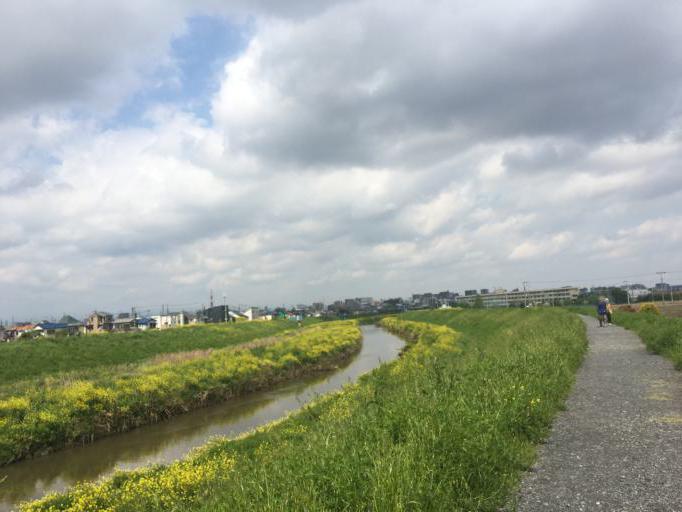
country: JP
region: Saitama
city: Kawagoe
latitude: 35.8970
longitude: 139.5039
